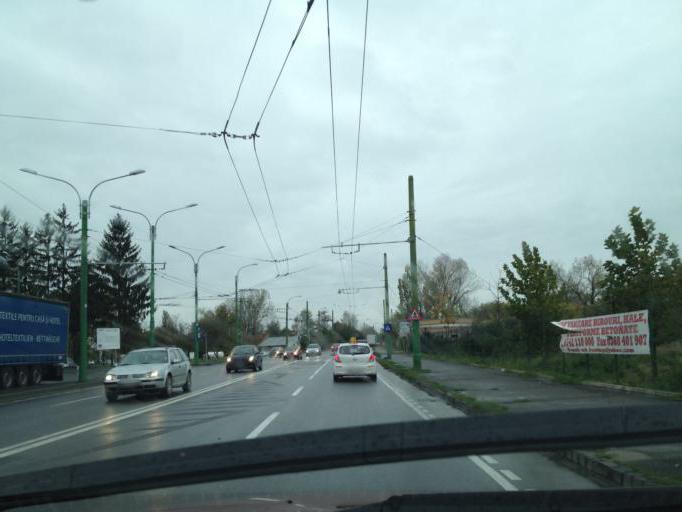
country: RO
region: Brasov
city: Brasov
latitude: 45.6819
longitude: 25.6154
